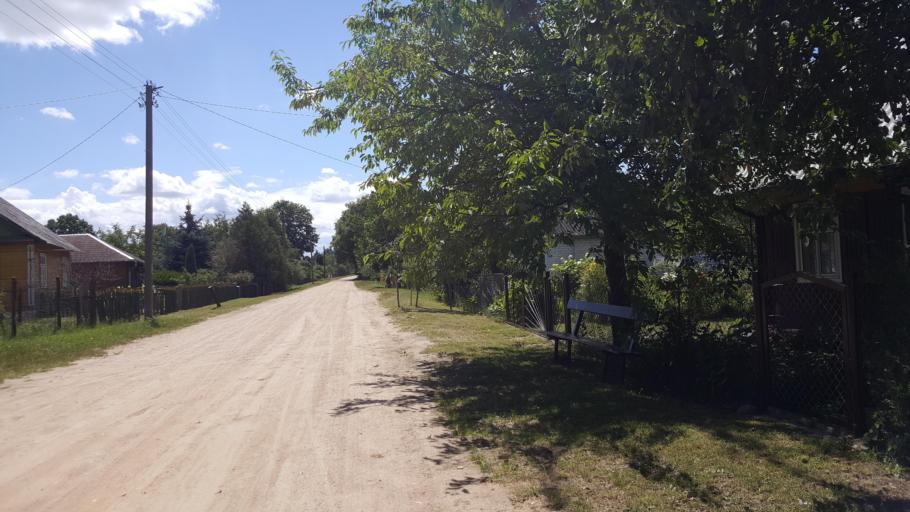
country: BY
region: Brest
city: Kamyanyets
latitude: 52.3139
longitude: 23.9185
